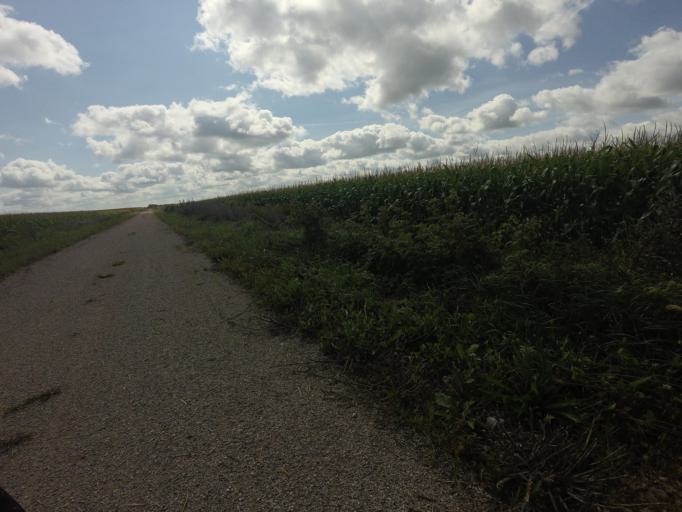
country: CA
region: Ontario
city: Huron East
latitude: 43.6456
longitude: -81.2158
